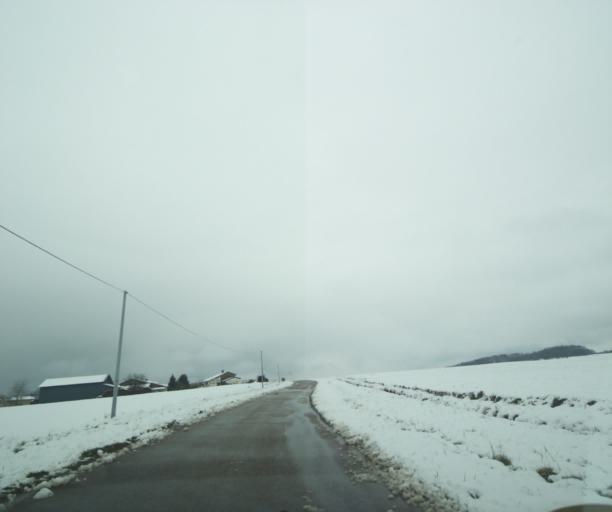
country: FR
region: Champagne-Ardenne
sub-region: Departement de la Haute-Marne
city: Montier-en-Der
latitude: 48.4359
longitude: 4.7985
